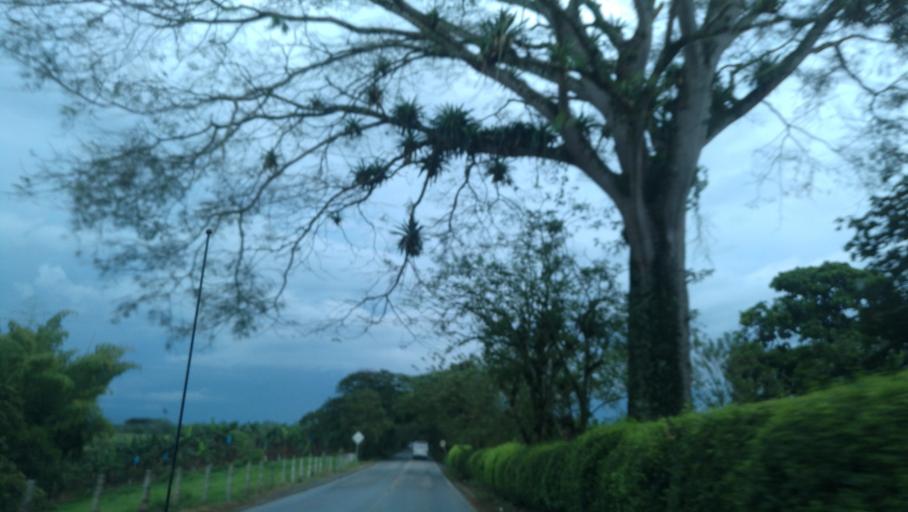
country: CO
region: Quindio
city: La Tebaida
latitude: 4.5086
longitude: -75.7697
